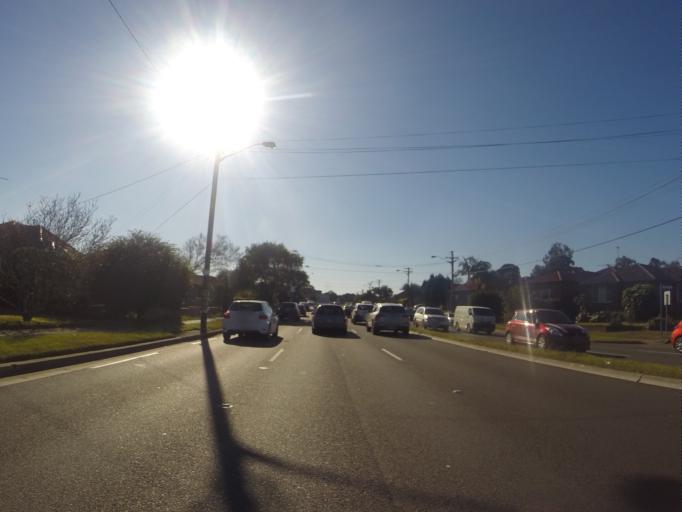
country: AU
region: New South Wales
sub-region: Canterbury
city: Roselands
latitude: -33.9328
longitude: 151.0731
